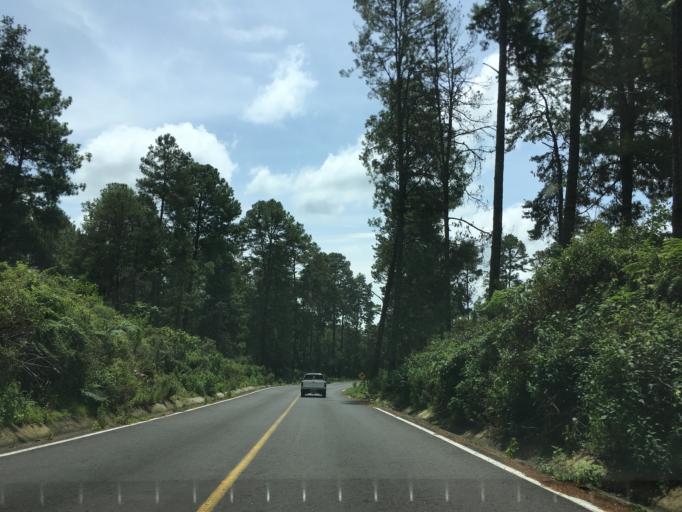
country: MX
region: Michoacan
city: Nuevo San Juan Parangaricutiro
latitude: 19.4461
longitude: -102.1717
